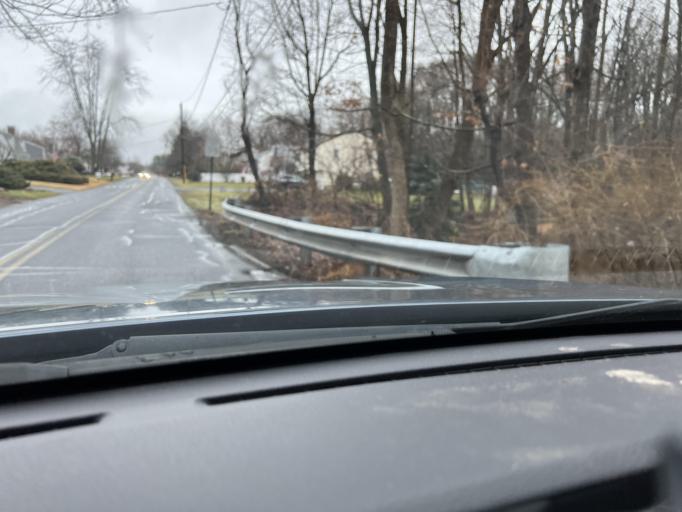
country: US
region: Massachusetts
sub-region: Hampden County
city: Southwick
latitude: 42.0415
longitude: -72.7000
